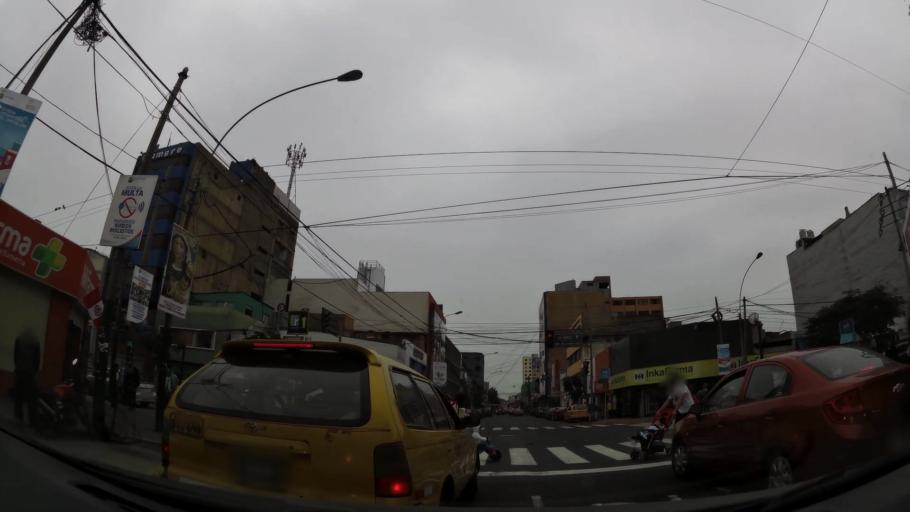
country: PE
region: Lima
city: Lima
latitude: -12.0737
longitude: -77.0494
